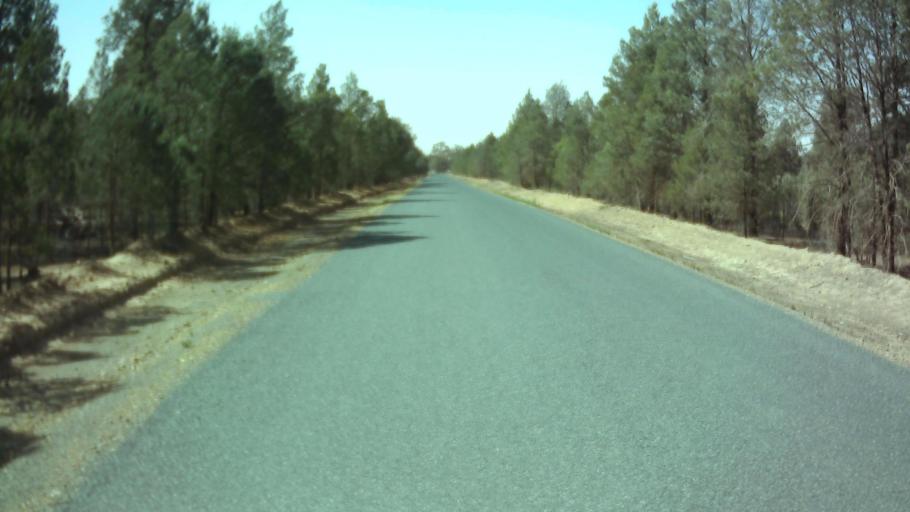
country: AU
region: New South Wales
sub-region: Weddin
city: Grenfell
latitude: -33.9042
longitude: 147.9201
